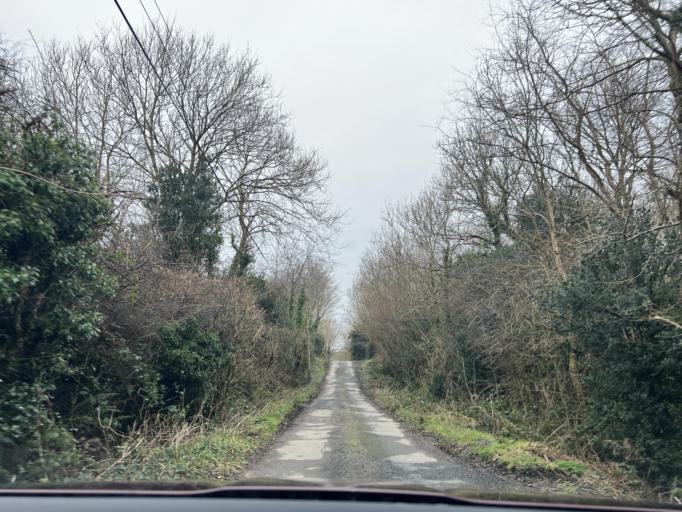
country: IE
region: Leinster
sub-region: Loch Garman
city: Castlebridge
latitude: 52.3836
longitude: -6.5513
